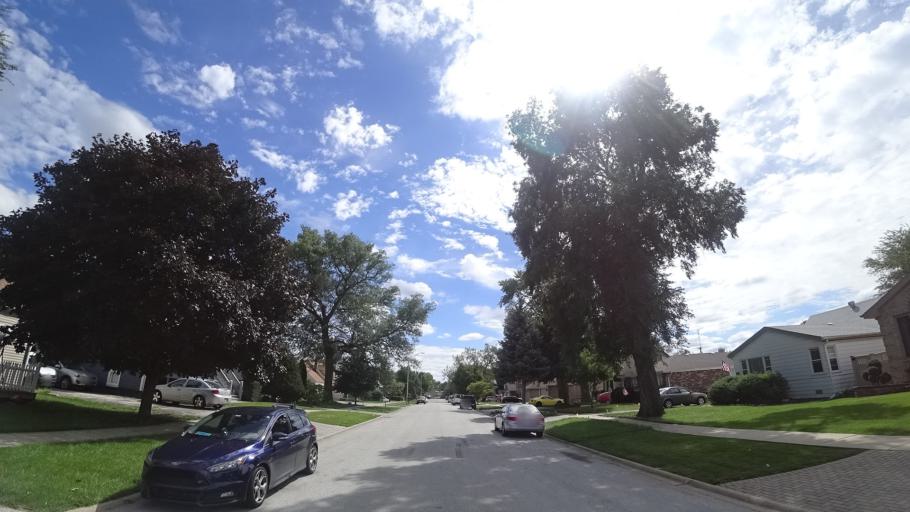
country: US
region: Illinois
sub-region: Cook County
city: Chicago Ridge
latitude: 41.7154
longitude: -87.7761
